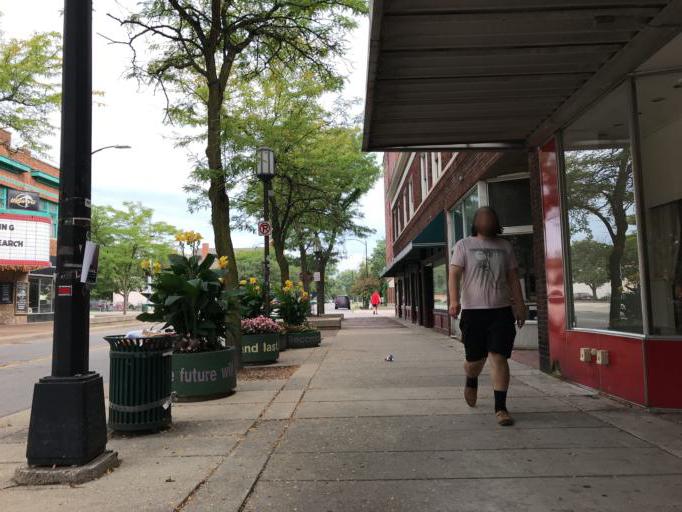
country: US
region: Michigan
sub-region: Washtenaw County
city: Ypsilanti
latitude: 42.2418
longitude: -83.6146
